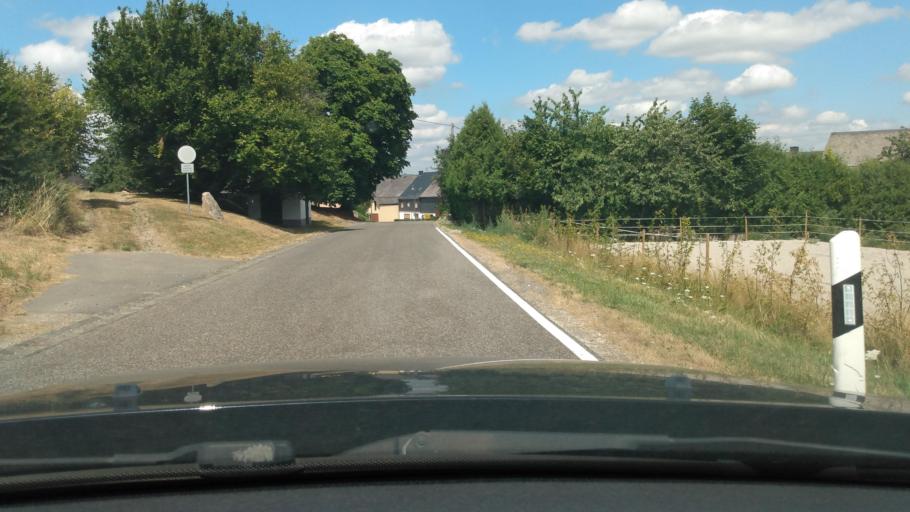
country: DE
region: Rheinland-Pfalz
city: Kleinich
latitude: 49.8833
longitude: 7.1728
